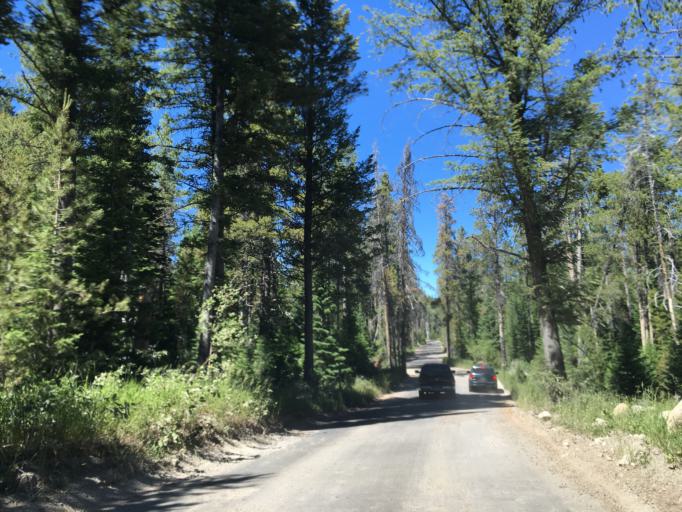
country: US
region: Wyoming
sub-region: Teton County
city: Moose Wilson Road
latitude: 43.6163
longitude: -110.7910
